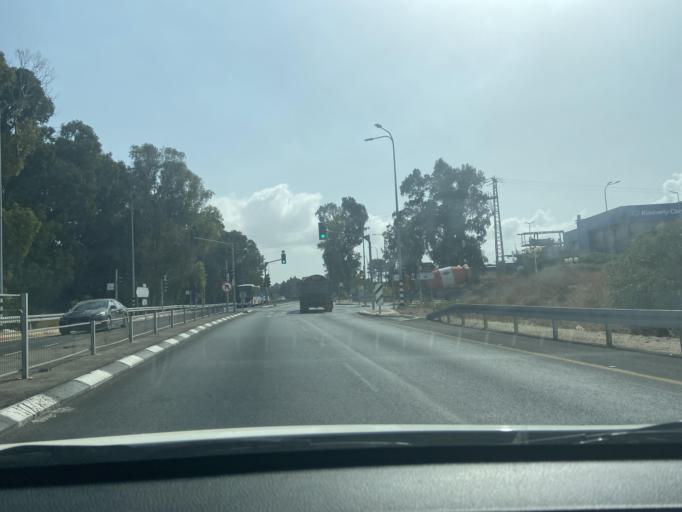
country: IL
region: Northern District
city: Nahariya
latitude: 33.0418
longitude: 35.1066
